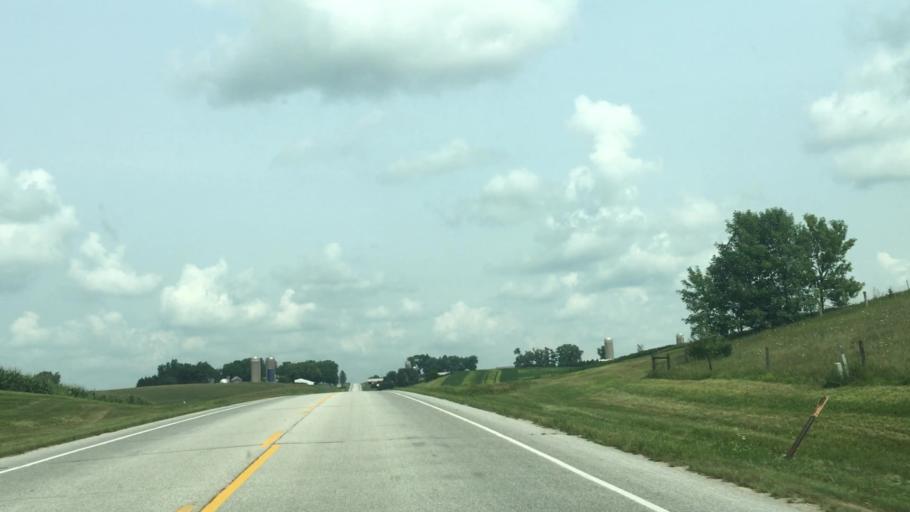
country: US
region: Minnesota
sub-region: Fillmore County
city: Harmony
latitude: 43.6087
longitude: -91.9297
